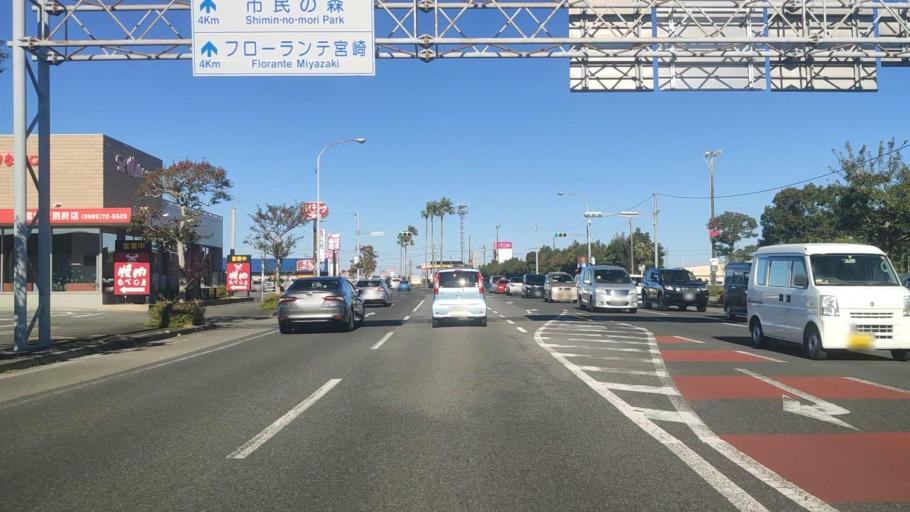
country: JP
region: Miyazaki
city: Miyazaki-shi
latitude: 31.9224
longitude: 131.4522
